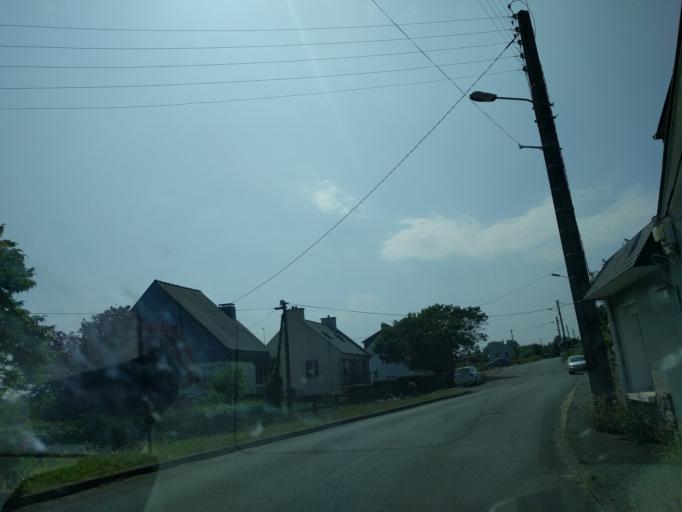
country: FR
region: Brittany
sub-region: Departement des Cotes-d'Armor
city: Plurien
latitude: 48.6385
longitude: -2.4273
